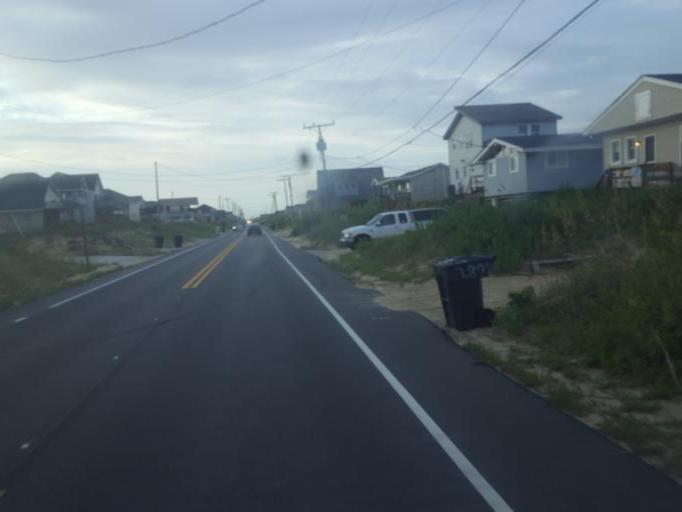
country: US
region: North Carolina
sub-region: Dare County
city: Kill Devil Hills
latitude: 36.0489
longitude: -75.6785
